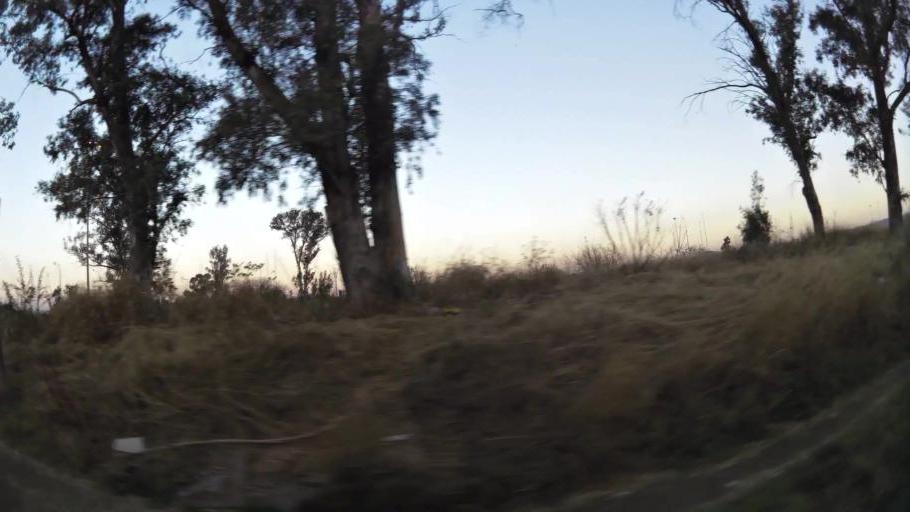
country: ZA
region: North-West
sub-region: Bojanala Platinum District Municipality
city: Rustenburg
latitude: -25.6592
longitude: 27.2360
